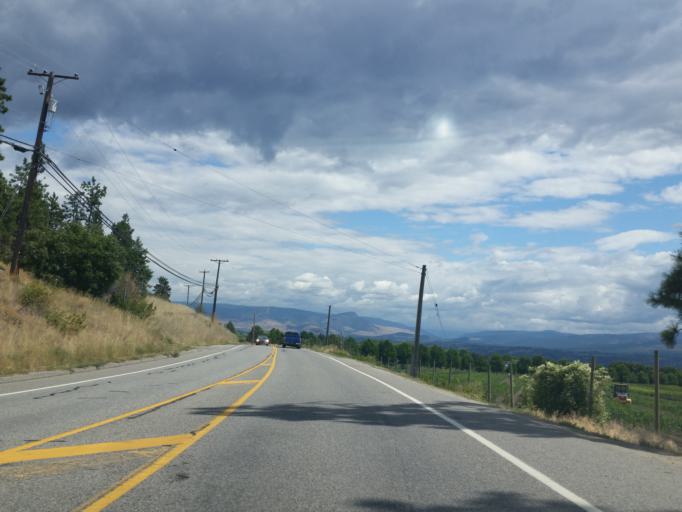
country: CA
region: British Columbia
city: West Kelowna
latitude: 49.8310
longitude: -119.5867
